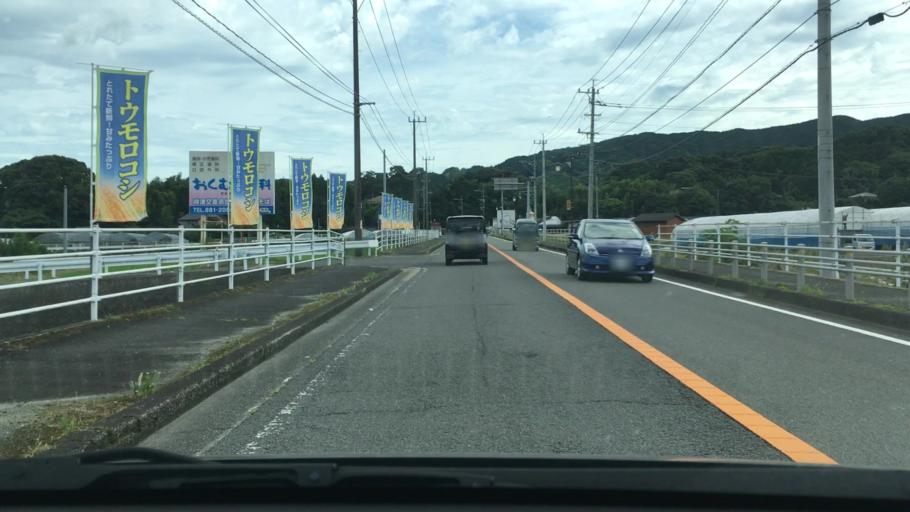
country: JP
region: Nagasaki
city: Togitsu
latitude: 32.9053
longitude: 129.7808
